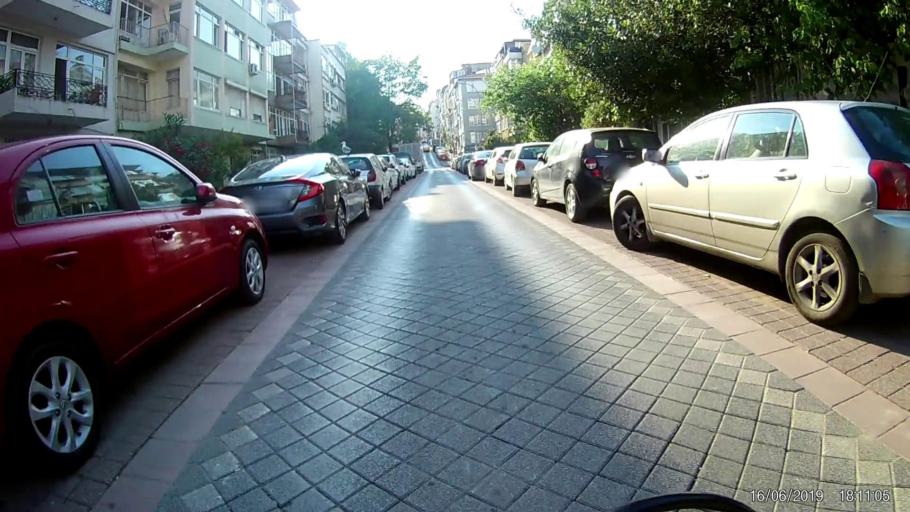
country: TR
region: Istanbul
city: UEskuedar
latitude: 40.9879
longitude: 29.0332
